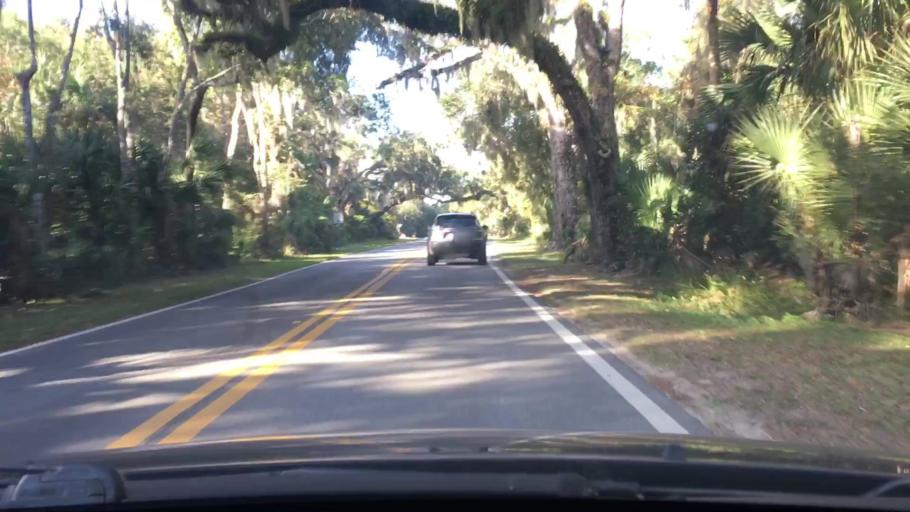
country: US
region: Florida
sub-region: Volusia County
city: Ormond-by-the-Sea
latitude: 29.3862
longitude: -81.1318
